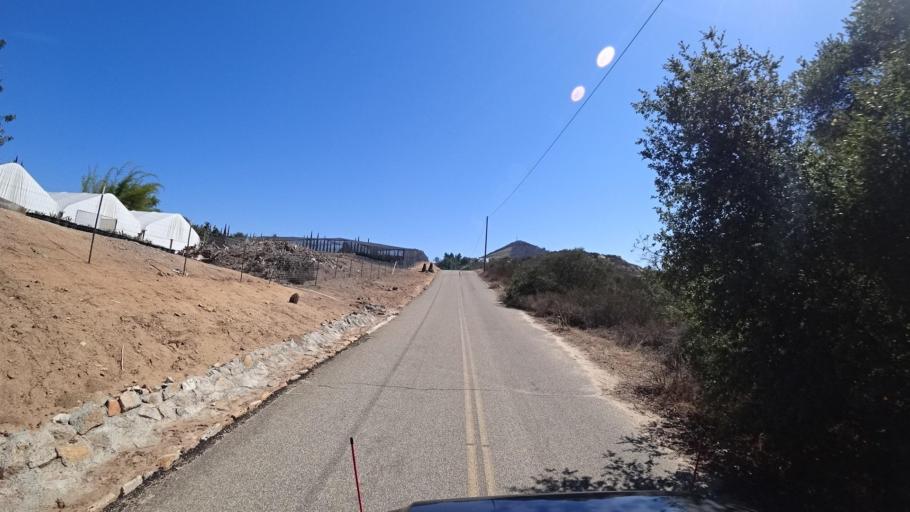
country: US
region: California
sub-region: San Diego County
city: Hidden Meadows
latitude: 33.2459
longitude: -117.0929
